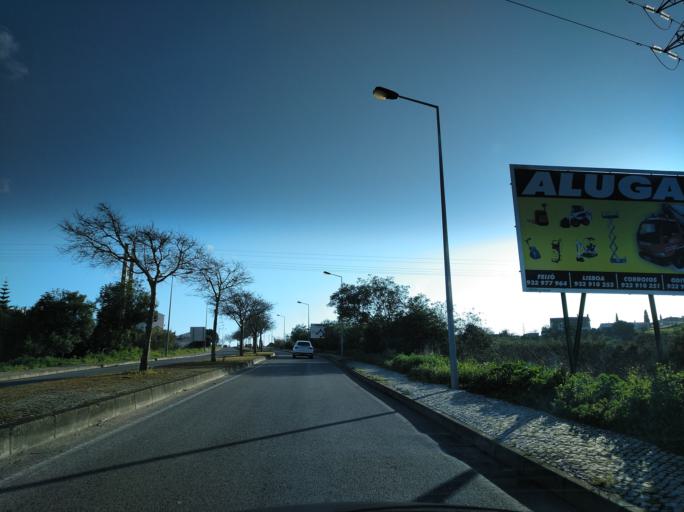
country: PT
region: Setubal
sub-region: Almada
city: Sobreda
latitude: 38.6583
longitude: -9.1882
